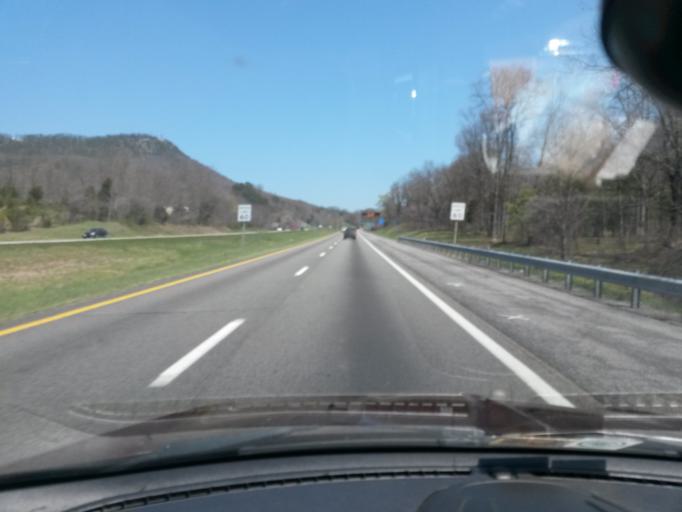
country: US
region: Virginia
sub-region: Roanoke County
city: Hollins
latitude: 37.3635
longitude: -79.9437
